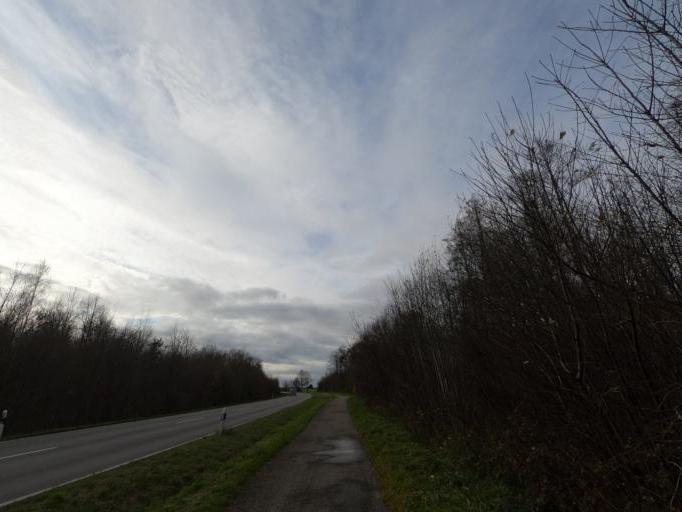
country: DE
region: Baden-Wuerttemberg
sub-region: Regierungsbezirk Stuttgart
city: Albershausen
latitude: 48.6845
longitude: 9.5438
